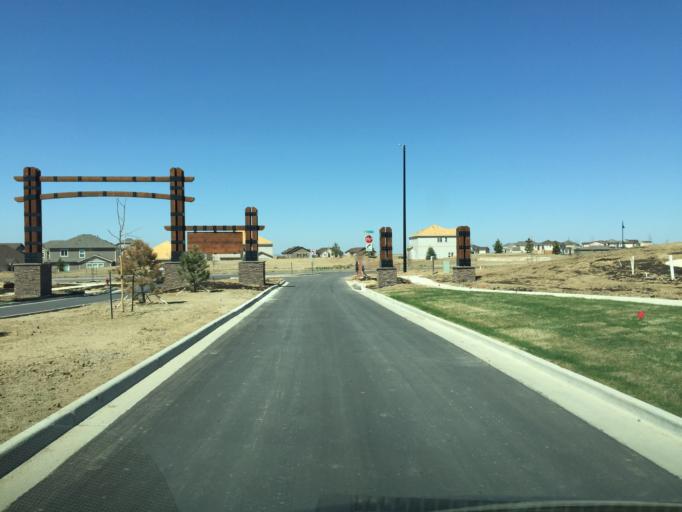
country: US
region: Colorado
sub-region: Boulder County
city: Erie
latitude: 40.0431
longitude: -105.0325
